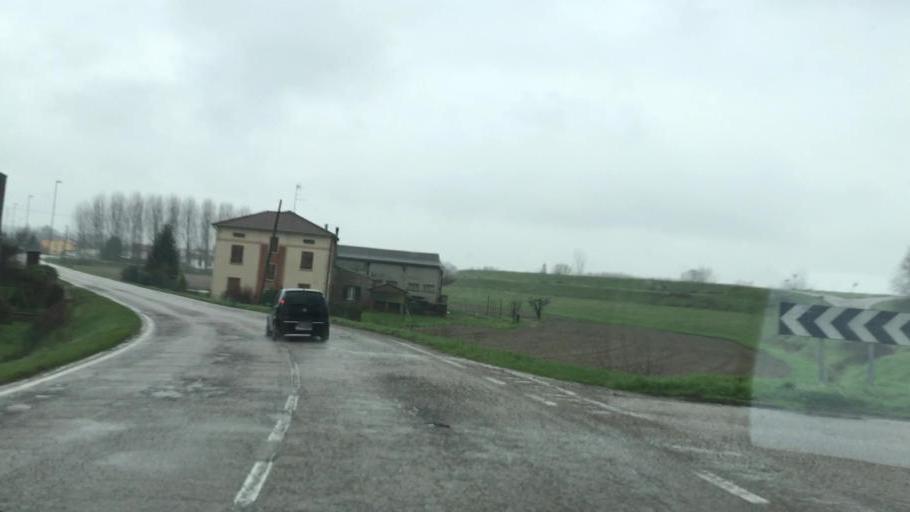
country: IT
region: Lombardy
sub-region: Provincia di Mantova
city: Borgofranco sul Po
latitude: 45.0451
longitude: 11.2134
